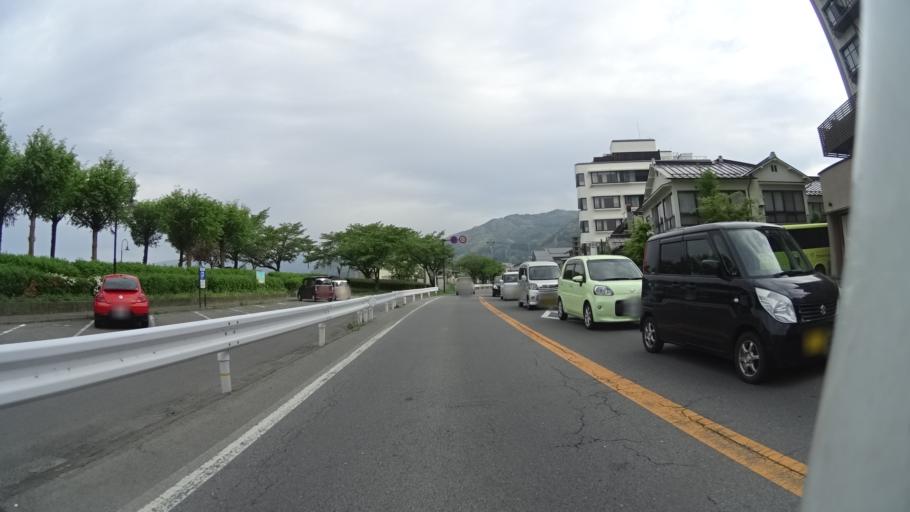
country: JP
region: Nagano
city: Suwa
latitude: 36.0519
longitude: 138.1128
